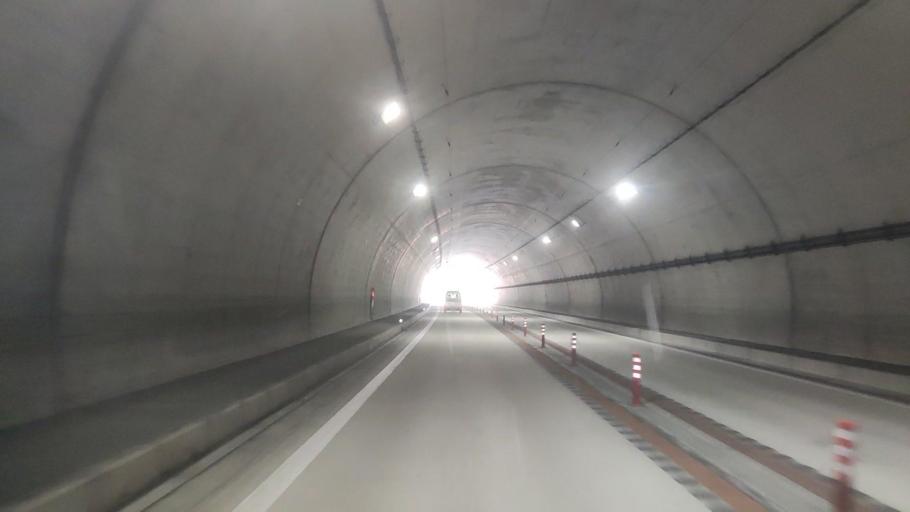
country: JP
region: Wakayama
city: Tanabe
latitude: 33.5848
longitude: 135.4490
